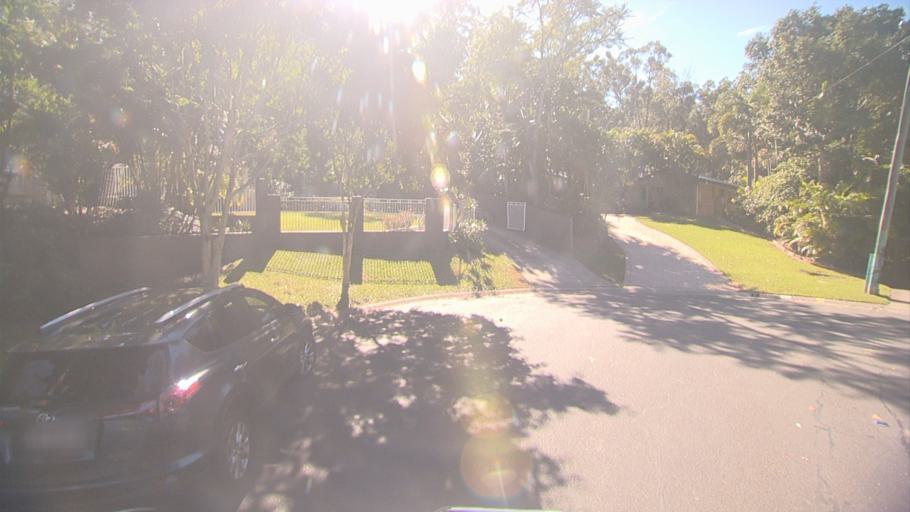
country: AU
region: Queensland
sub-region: Logan
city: Slacks Creek
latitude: -27.6380
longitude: 153.1642
